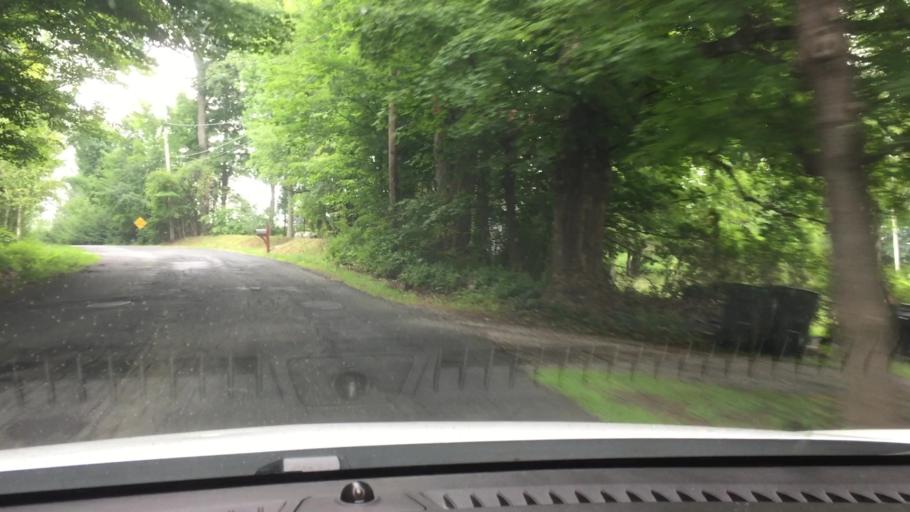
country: US
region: Massachusetts
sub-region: Berkshire County
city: Lee
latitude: 42.3019
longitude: -73.2802
